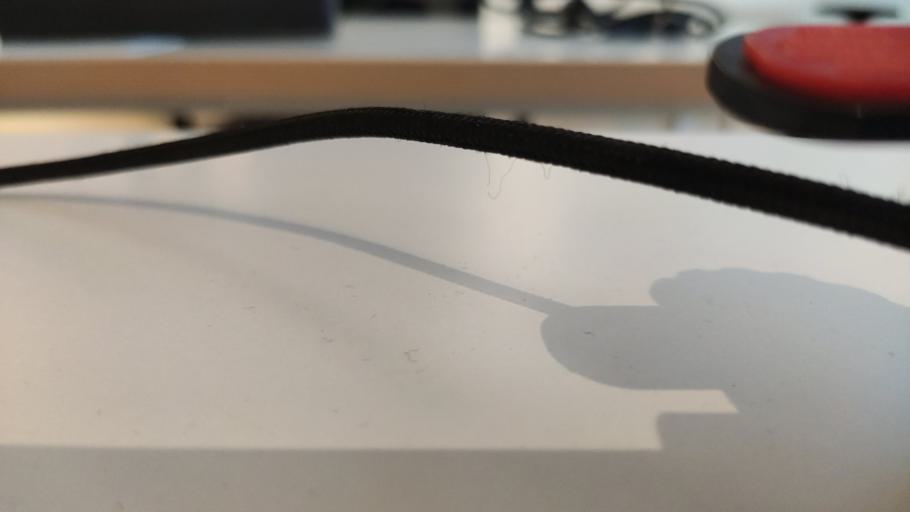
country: RU
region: Moskovskaya
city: Novopetrovskoye
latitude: 55.8977
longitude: 36.4322
